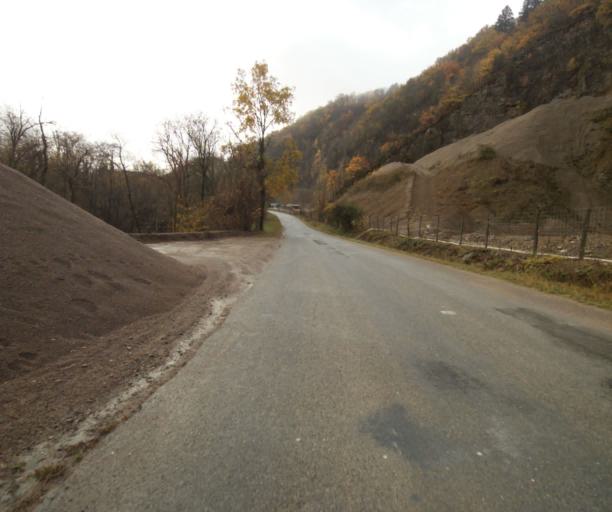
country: FR
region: Limousin
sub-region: Departement de la Correze
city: Cornil
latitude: 45.1930
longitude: 1.6506
